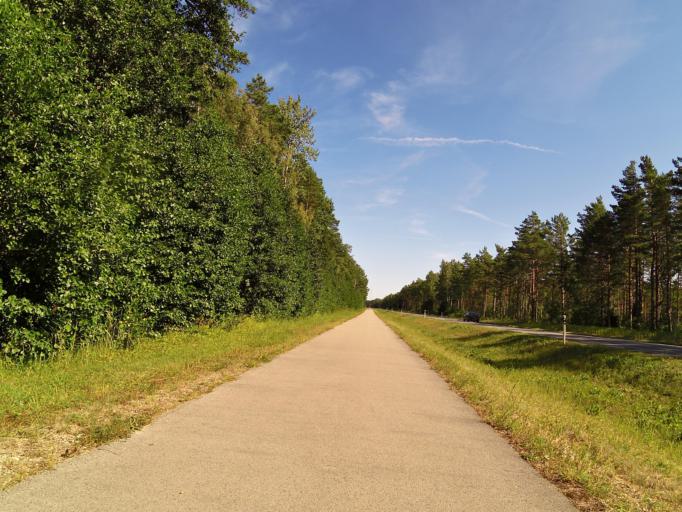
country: EE
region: Hiiumaa
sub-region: Kaerdla linn
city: Kardla
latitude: 59.0032
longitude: 22.6925
